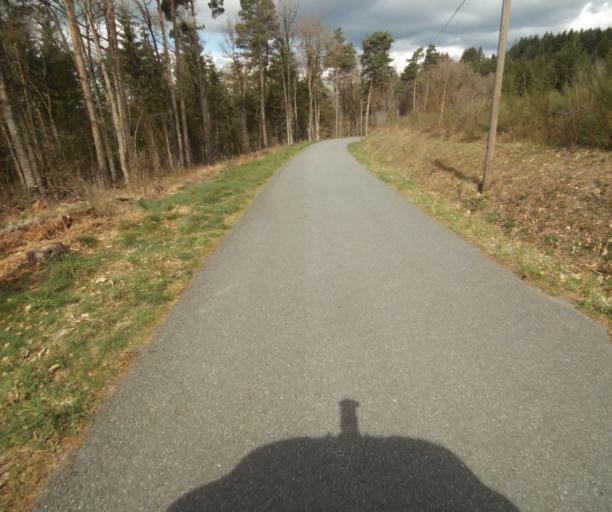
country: FR
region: Limousin
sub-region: Departement de la Correze
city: Correze
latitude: 45.3878
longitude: 1.9173
